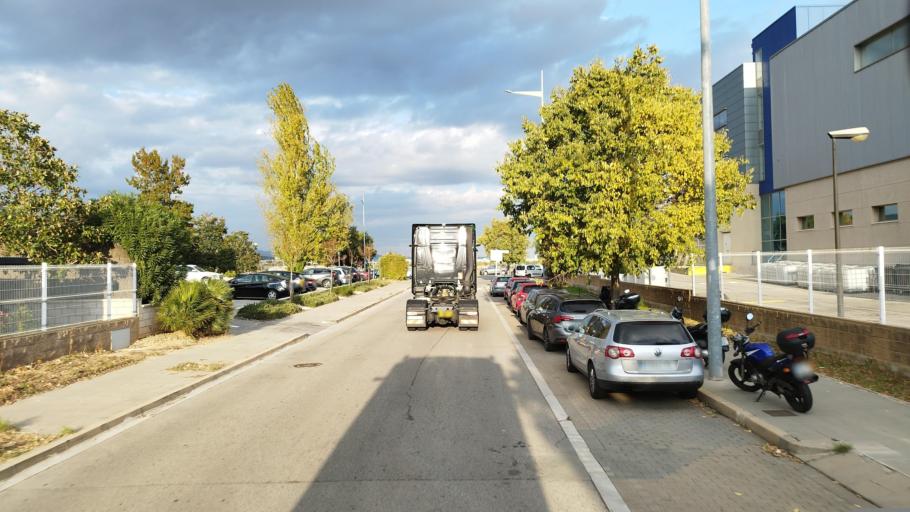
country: ES
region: Catalonia
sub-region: Provincia de Barcelona
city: Gava
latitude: 41.2876
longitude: 1.9945
